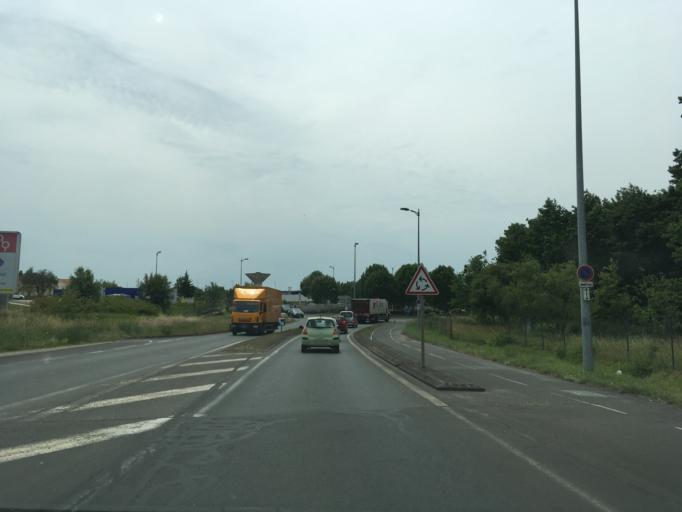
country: FR
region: Poitou-Charentes
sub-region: Departement des Deux-Sevres
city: Bessines
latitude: 46.3203
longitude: -0.4917
